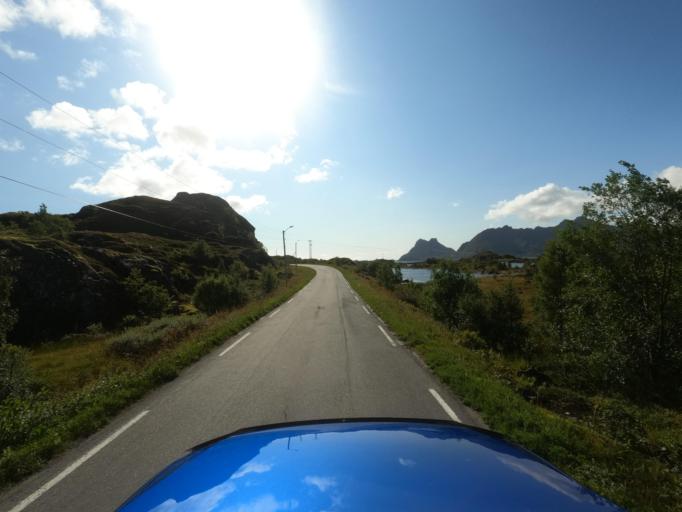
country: NO
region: Nordland
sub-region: Vestvagoy
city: Evjen
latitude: 68.1281
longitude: 13.7764
